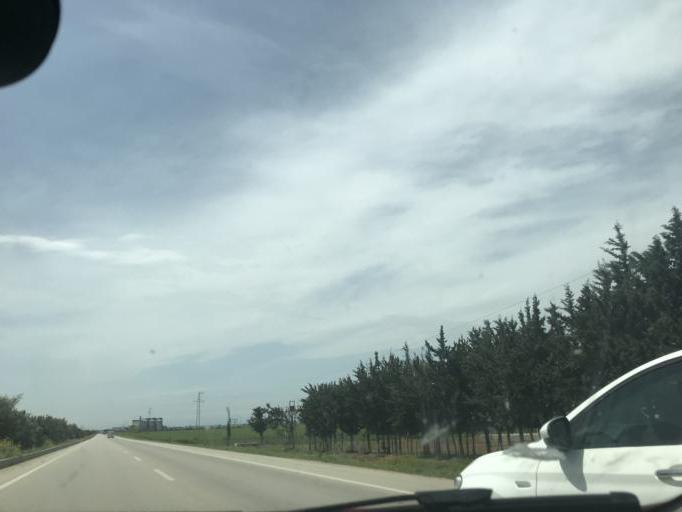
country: TR
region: Adana
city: Yuregir
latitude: 36.9760
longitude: 35.4846
